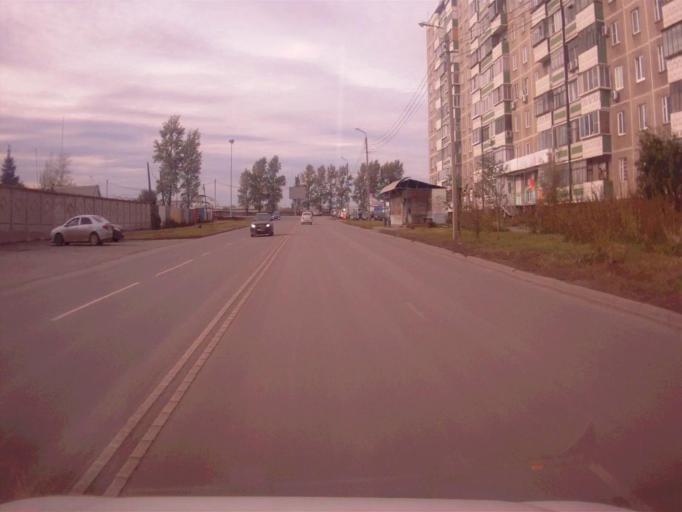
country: RU
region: Chelyabinsk
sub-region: Gorod Chelyabinsk
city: Chelyabinsk
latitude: 55.1179
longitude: 61.4218
